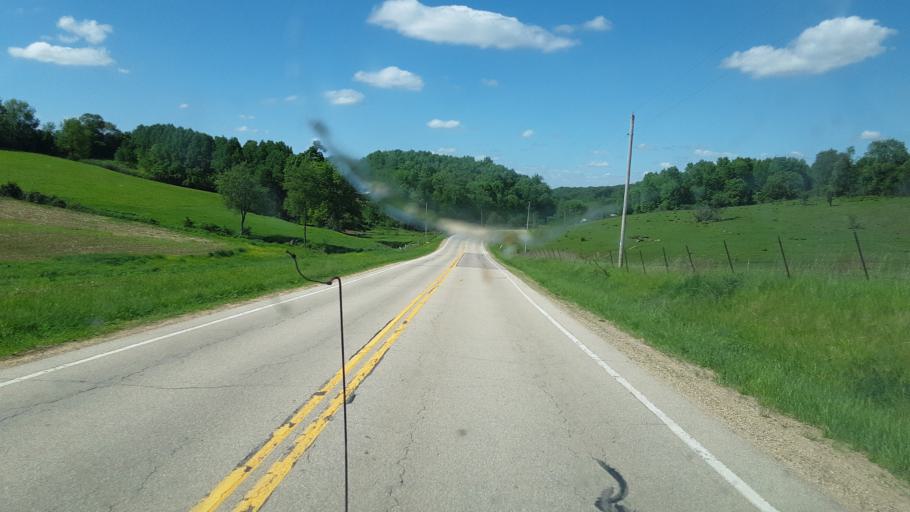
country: US
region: Wisconsin
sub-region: Sauk County
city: Reedsburg
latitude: 43.4807
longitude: -90.2046
